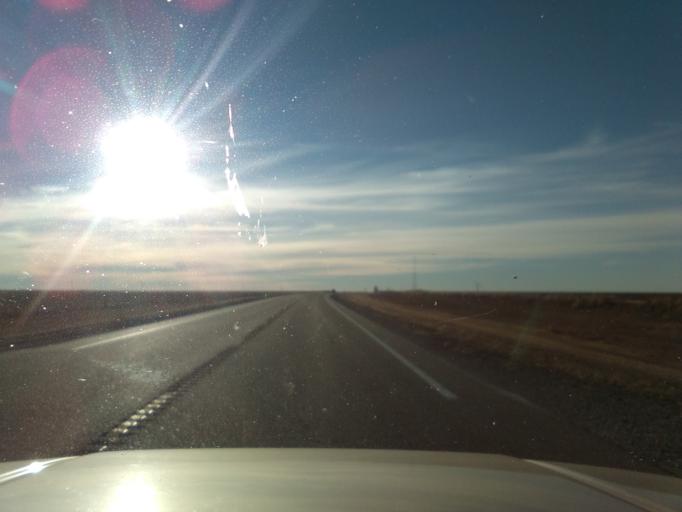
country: US
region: Kansas
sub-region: Sheridan County
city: Hoxie
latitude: 39.4858
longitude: -100.7023
